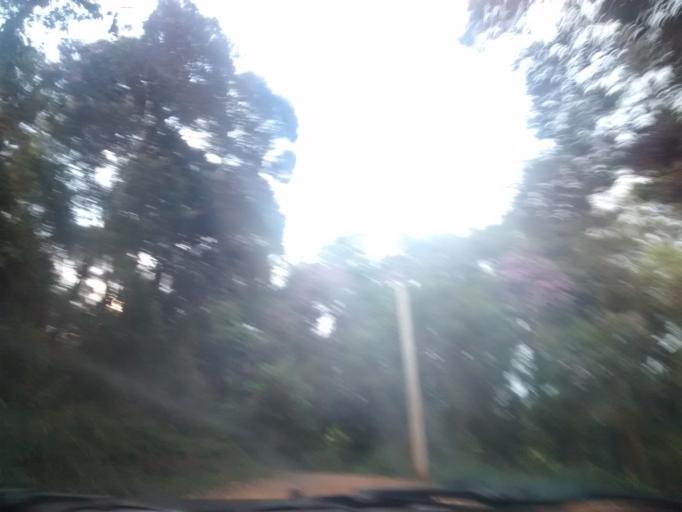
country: BR
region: Sao Paulo
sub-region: Campos Do Jordao
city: Campos do Jordao
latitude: -22.6816
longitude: -45.6364
